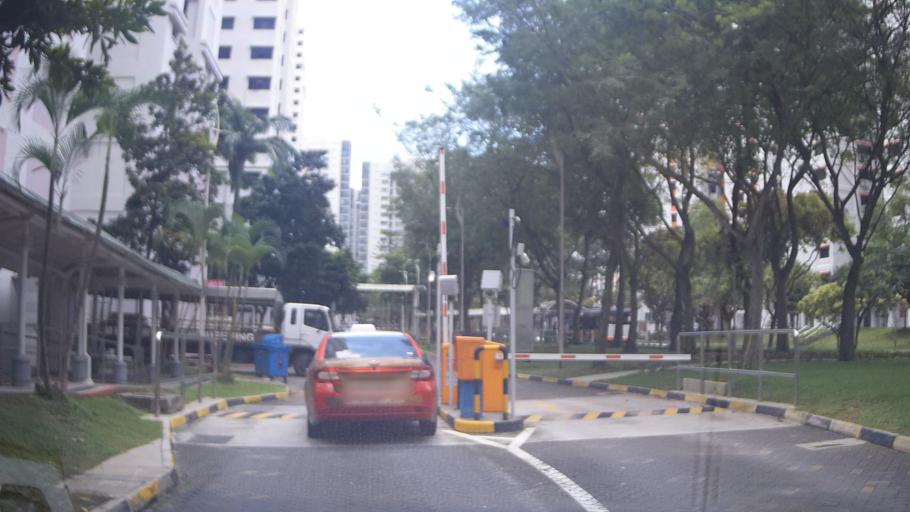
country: MY
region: Johor
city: Johor Bahru
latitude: 1.4020
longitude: 103.7516
